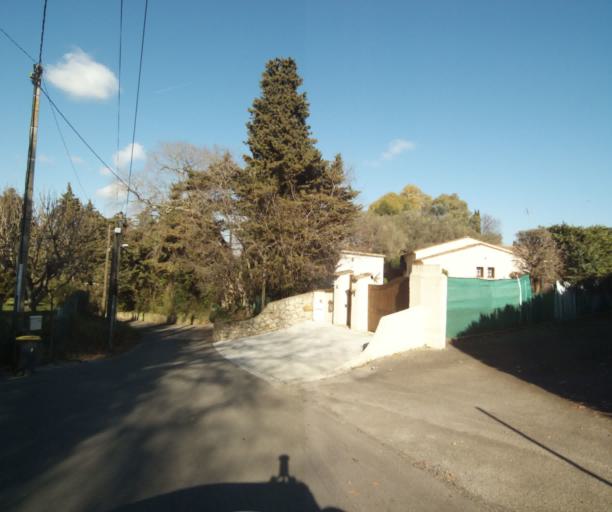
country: FR
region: Provence-Alpes-Cote d'Azur
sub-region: Departement des Alpes-Maritimes
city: Biot
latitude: 43.6132
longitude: 7.1037
